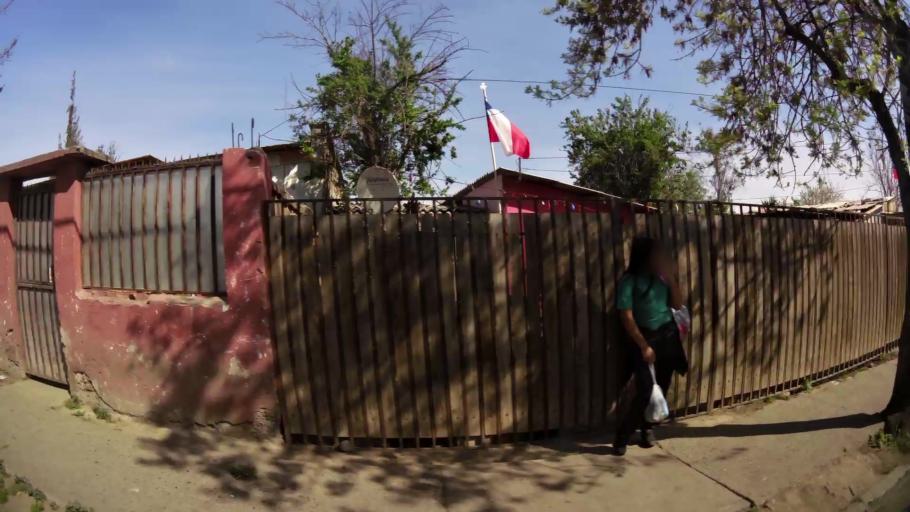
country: CL
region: Santiago Metropolitan
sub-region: Provincia de Santiago
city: La Pintana
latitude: -33.5379
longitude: -70.6228
